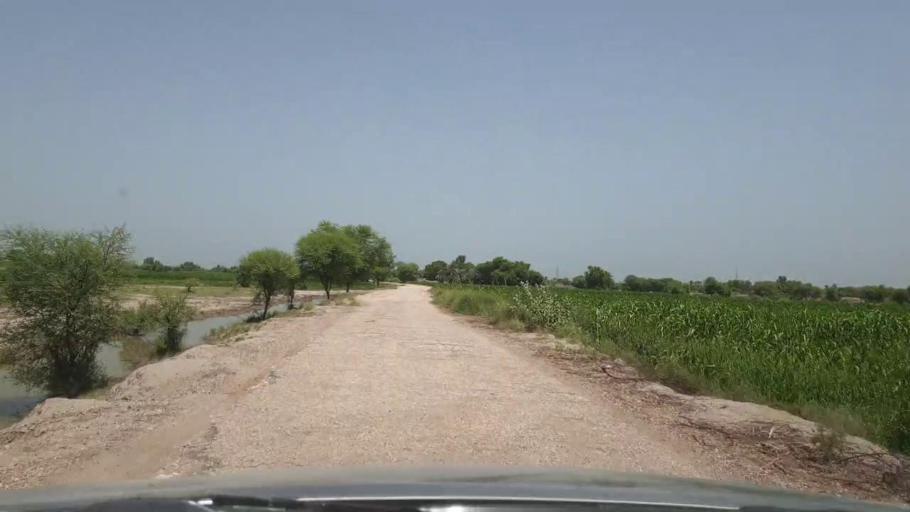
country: PK
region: Sindh
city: Pano Aqil
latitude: 27.8306
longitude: 69.2022
